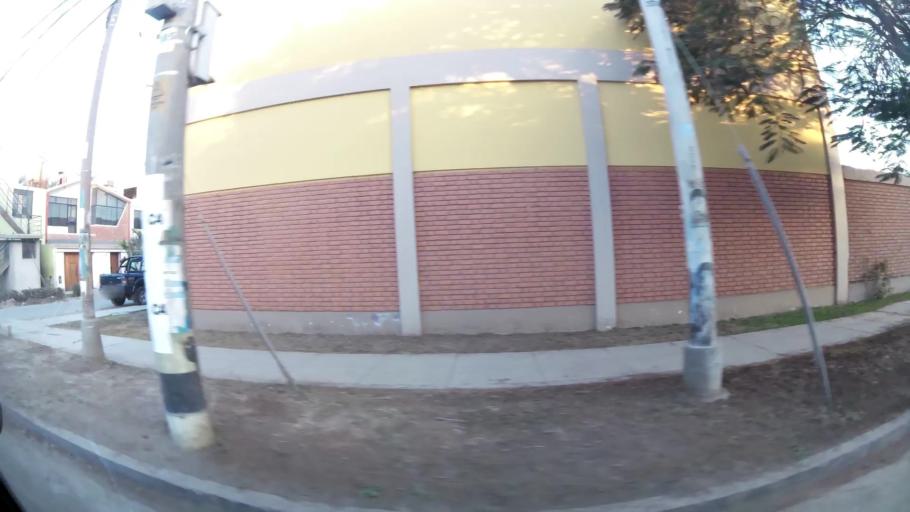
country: PE
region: Ica
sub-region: Provincia de Ica
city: Ica
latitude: -14.0760
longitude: -75.7281
